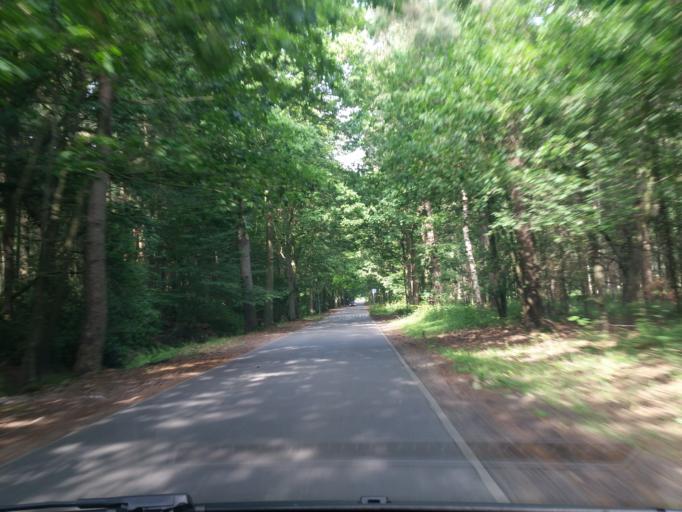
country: BE
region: Flanders
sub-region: Provincie Antwerpen
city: Brasschaat
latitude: 51.3123
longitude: 4.5408
